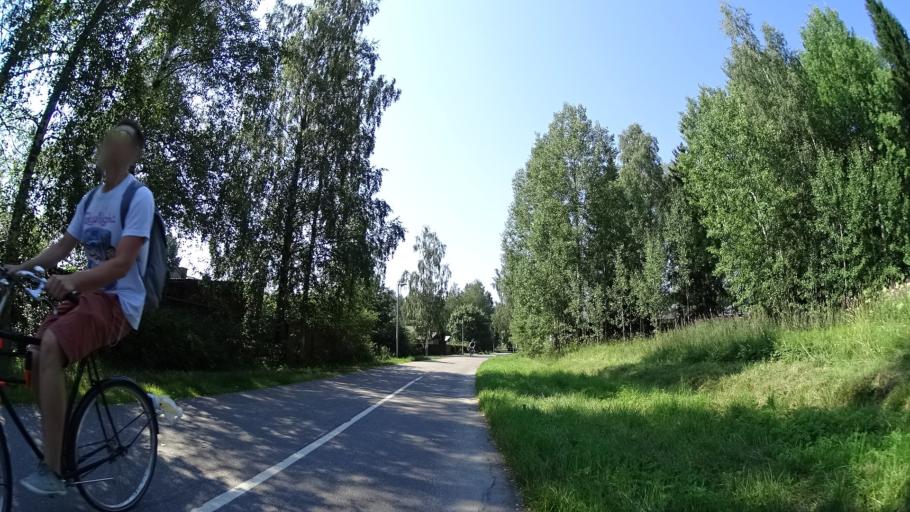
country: FI
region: Uusimaa
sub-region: Helsinki
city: Kerava
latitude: 60.3946
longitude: 25.0960
